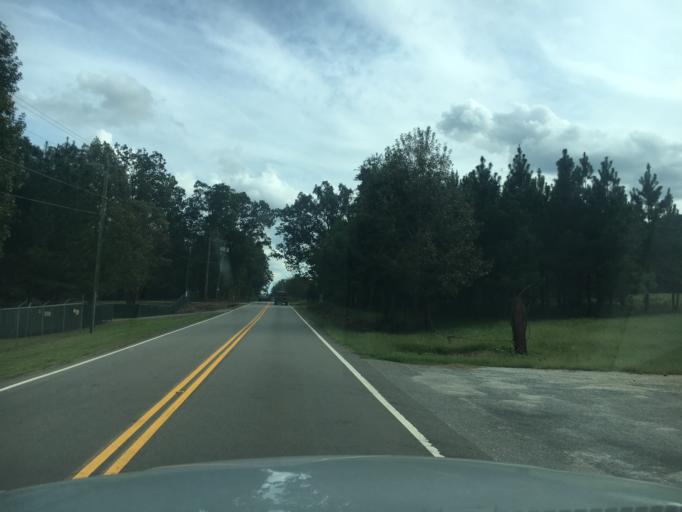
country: US
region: South Carolina
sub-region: Spartanburg County
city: Wellford
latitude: 34.9212
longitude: -82.0619
